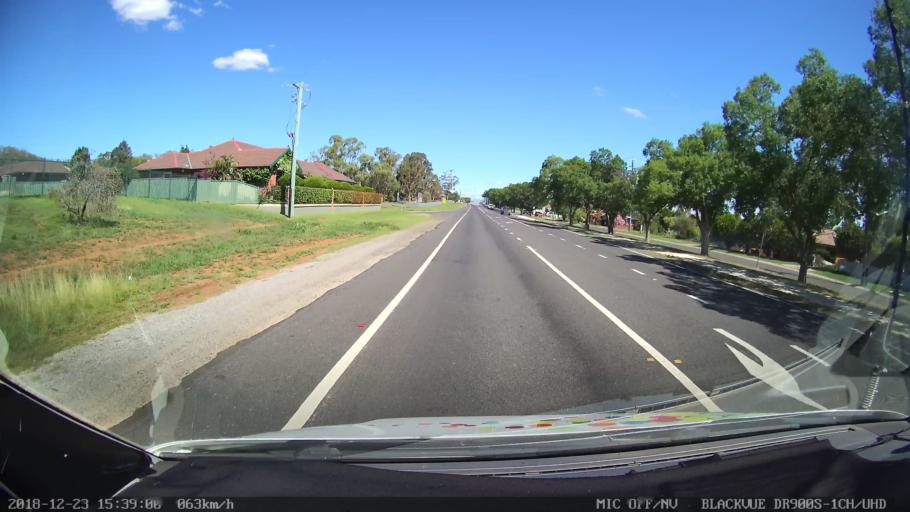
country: AU
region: New South Wales
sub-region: Tamworth Municipality
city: Tamworth
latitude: -31.0626
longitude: 150.9007
